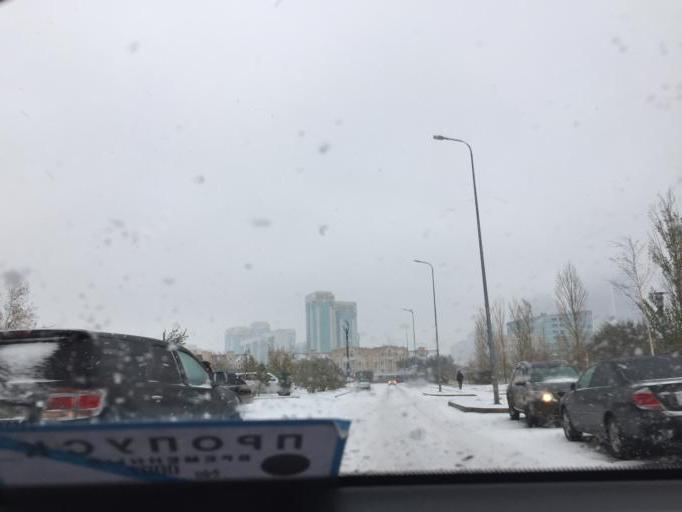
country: KZ
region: Astana Qalasy
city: Astana
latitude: 51.1396
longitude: 71.4147
